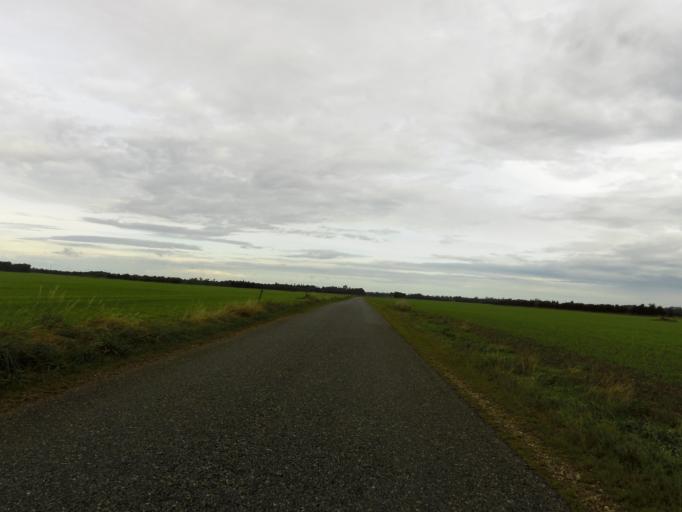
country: DK
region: South Denmark
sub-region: Esbjerg Kommune
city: Ribe
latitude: 55.2666
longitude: 8.8229
